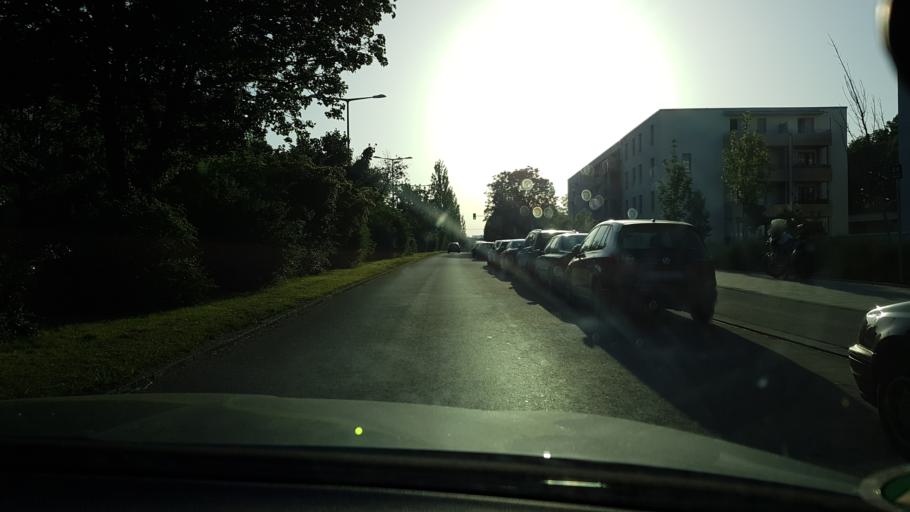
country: DE
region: Bavaria
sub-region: Upper Bavaria
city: Unterfoehring
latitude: 48.1680
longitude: 11.6415
